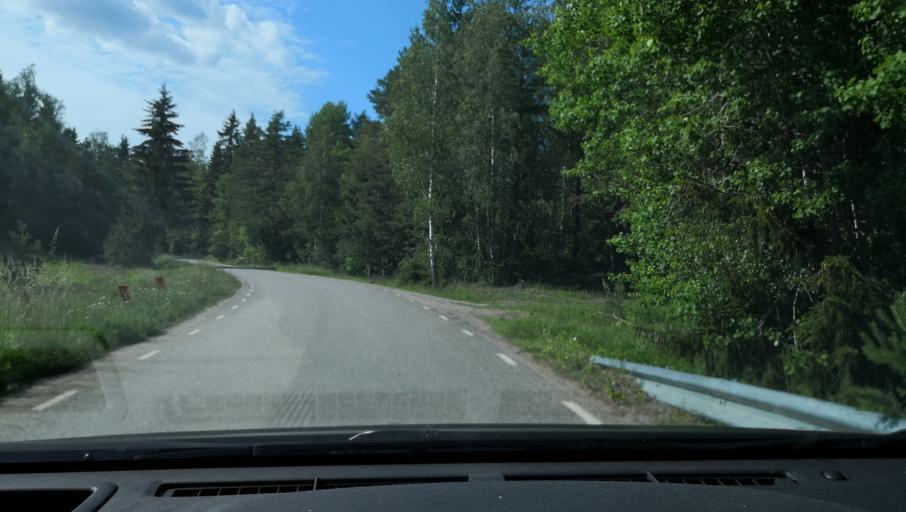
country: SE
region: Uppsala
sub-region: Enkopings Kommun
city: Orsundsbro
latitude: 59.8409
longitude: 17.2020
